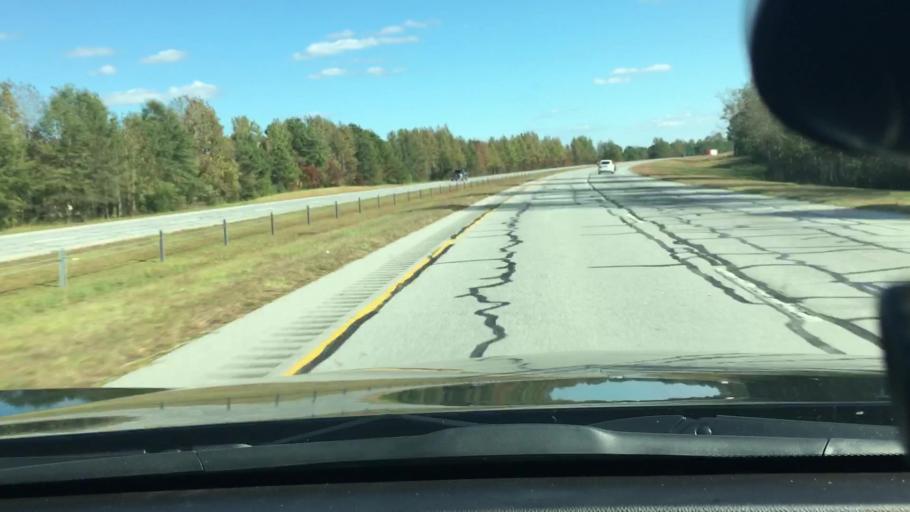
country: US
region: North Carolina
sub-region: Pitt County
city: Farmville
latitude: 35.6198
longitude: -77.5926
